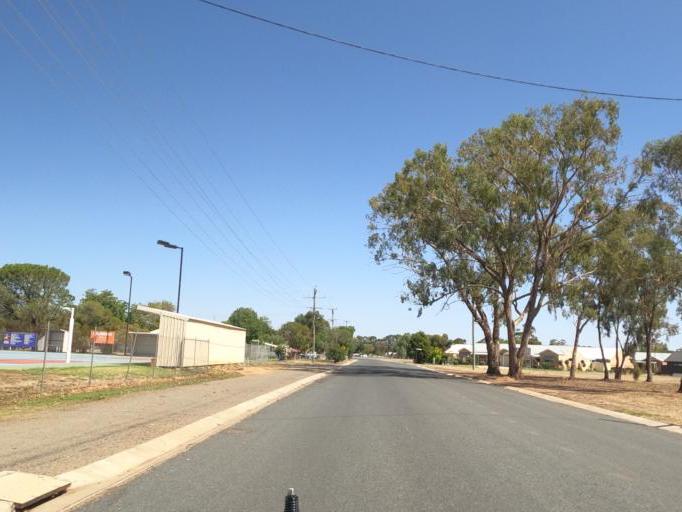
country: AU
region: New South Wales
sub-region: Corowa Shire
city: Mulwala
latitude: -35.9876
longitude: 146.0023
